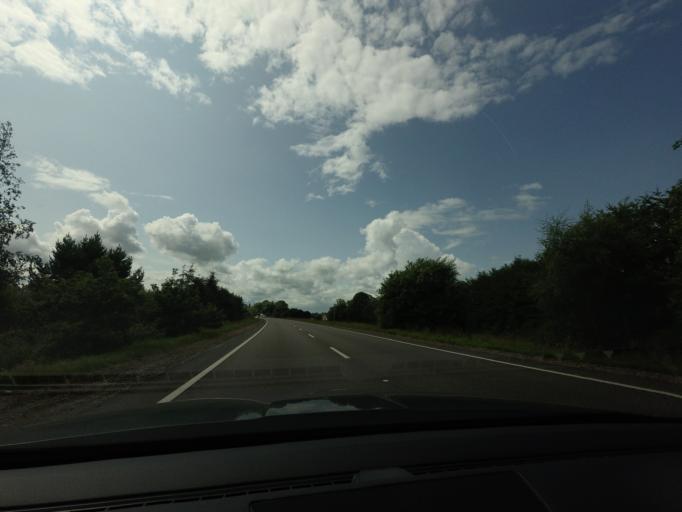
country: GB
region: Scotland
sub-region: Moray
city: Forres
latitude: 57.6156
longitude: -3.6059
